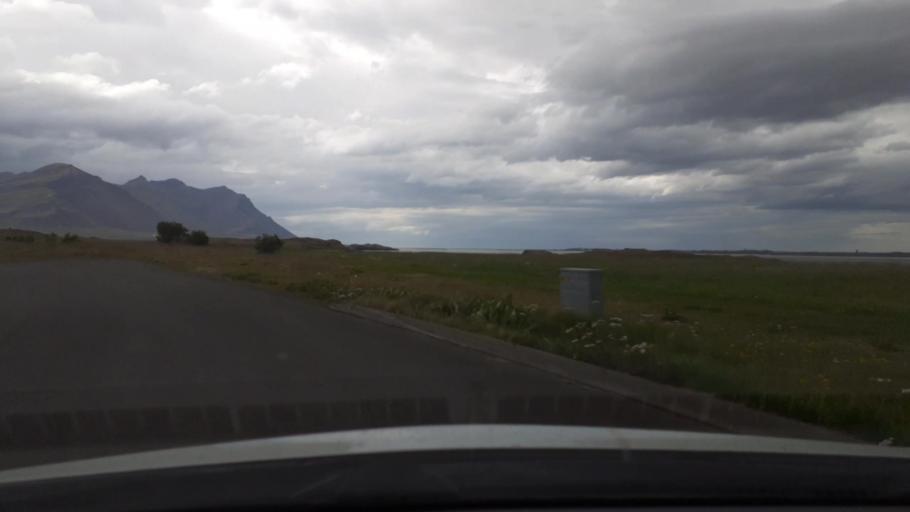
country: IS
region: West
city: Borgarnes
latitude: 64.5626
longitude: -21.7705
